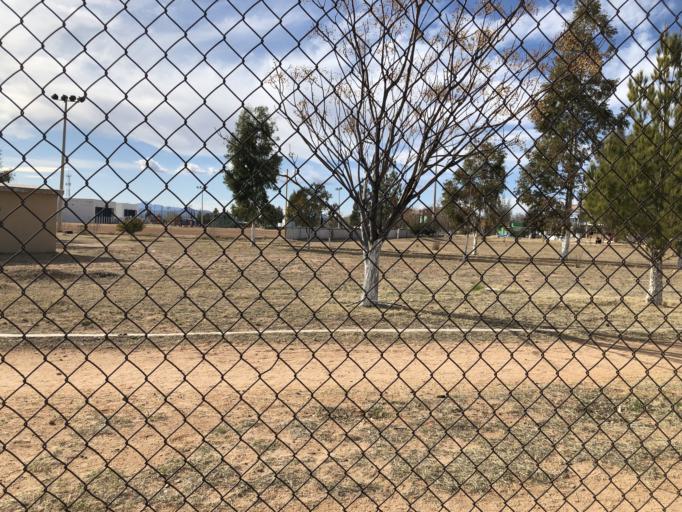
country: MX
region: Sonora
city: Agua Prieta
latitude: 31.3291
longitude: -109.5240
